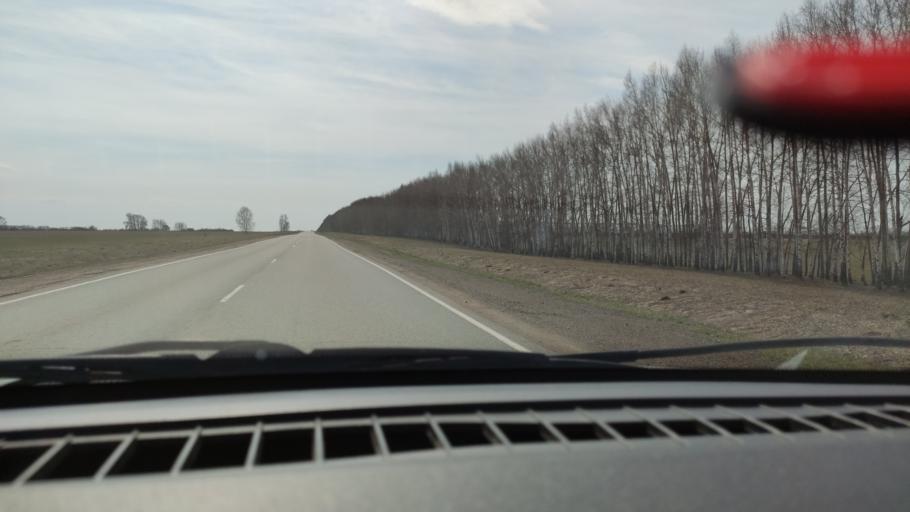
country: RU
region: Bashkortostan
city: Dyurtyuli
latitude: 55.4486
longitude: 54.8004
